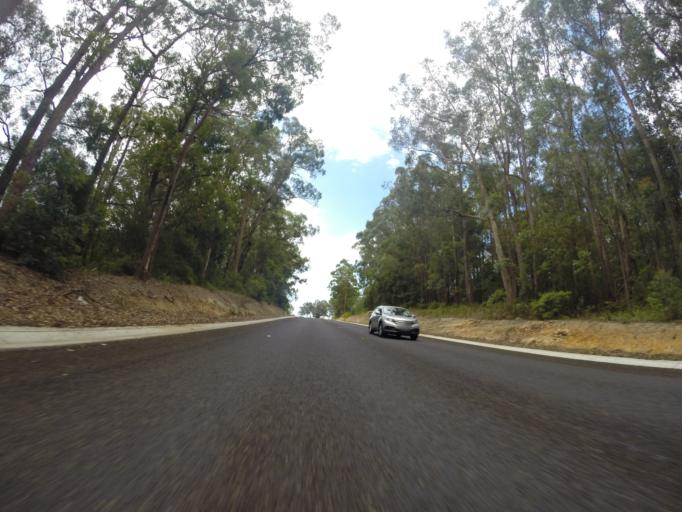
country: AU
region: New South Wales
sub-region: Shoalhaven Shire
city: Milton
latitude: -35.2263
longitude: 150.4355
